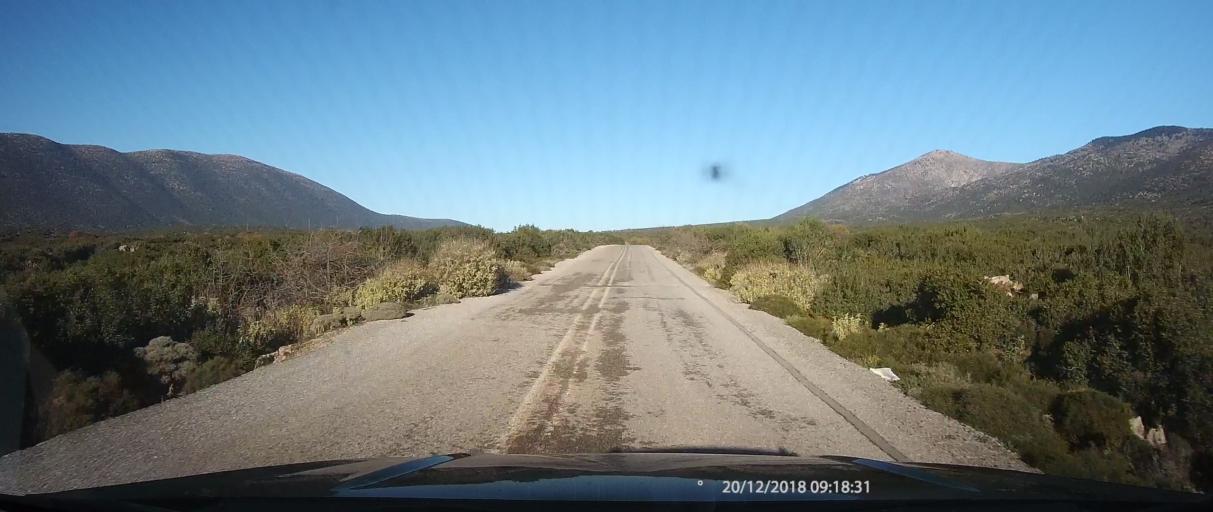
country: GR
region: Peloponnese
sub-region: Nomos Lakonias
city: Molaoi
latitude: 36.9117
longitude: 22.9534
